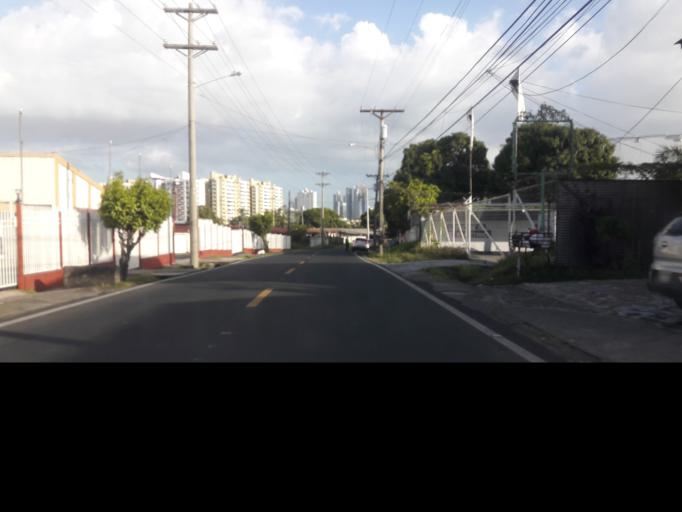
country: PA
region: Panama
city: San Miguelito
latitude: 9.0238
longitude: -79.4944
